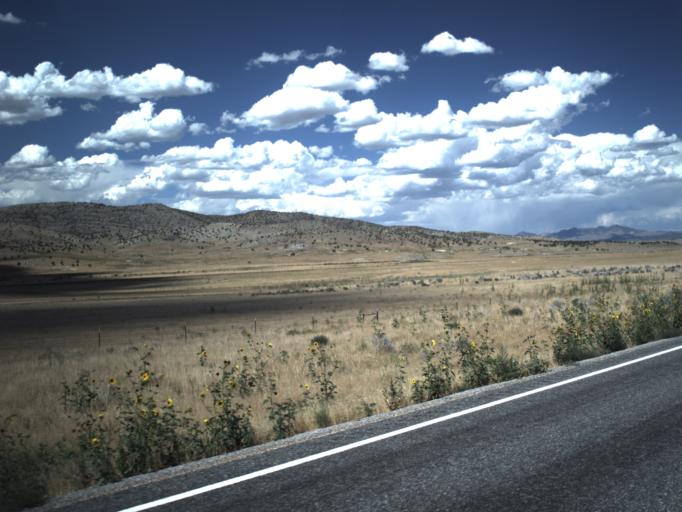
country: US
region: Utah
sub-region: Millard County
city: Delta
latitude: 39.6507
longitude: -112.2948
